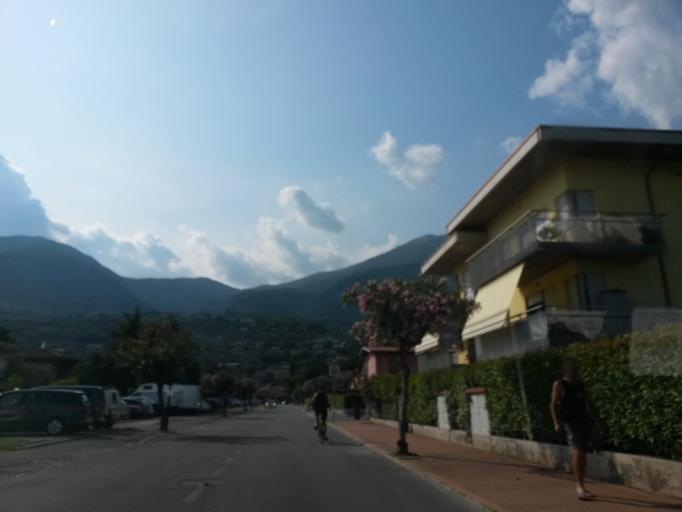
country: IT
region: Lombardy
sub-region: Provincia di Brescia
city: Toscolano Maderno
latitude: 45.6343
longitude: 10.6090
